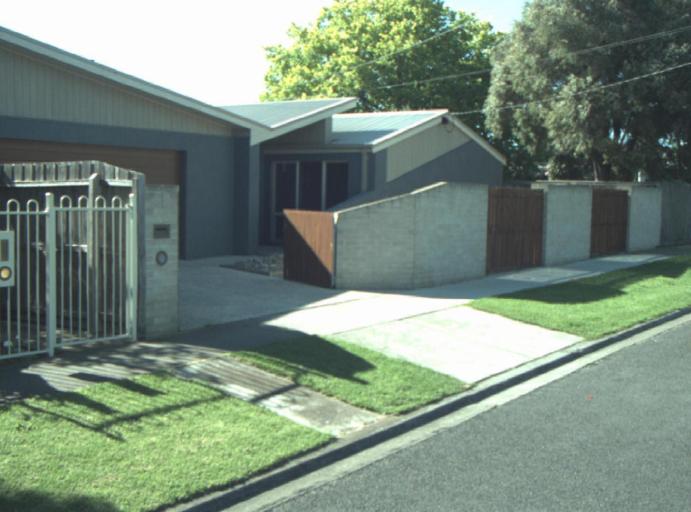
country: AU
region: Victoria
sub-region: Greater Geelong
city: Bell Post Hill
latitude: -38.0950
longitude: 144.3240
